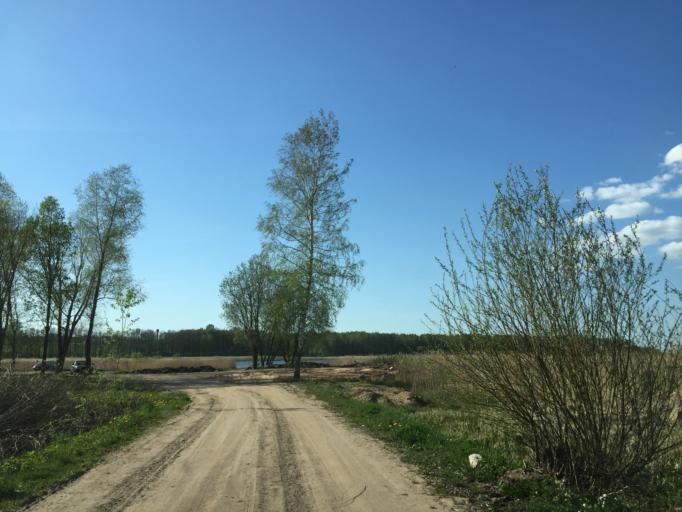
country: LV
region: Limbazu Rajons
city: Limbazi
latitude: 57.5193
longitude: 24.7040
